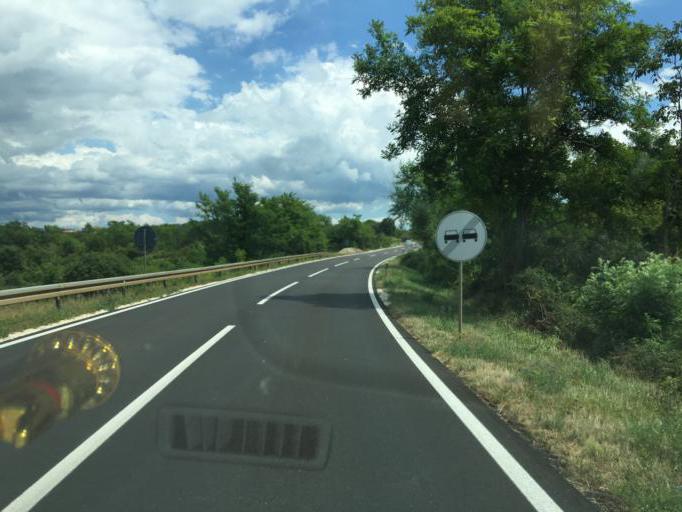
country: HR
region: Istarska
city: Karojba
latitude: 45.2443
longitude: 13.8591
